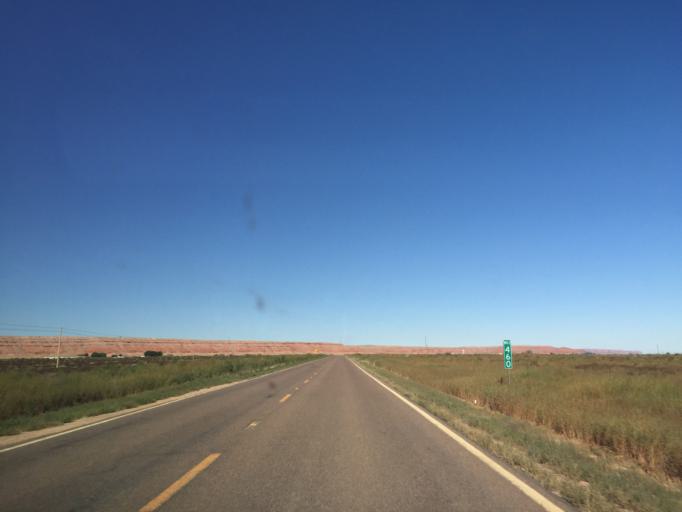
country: US
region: Arizona
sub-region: Apache County
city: Many Farms
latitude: 36.3293
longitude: -109.6212
